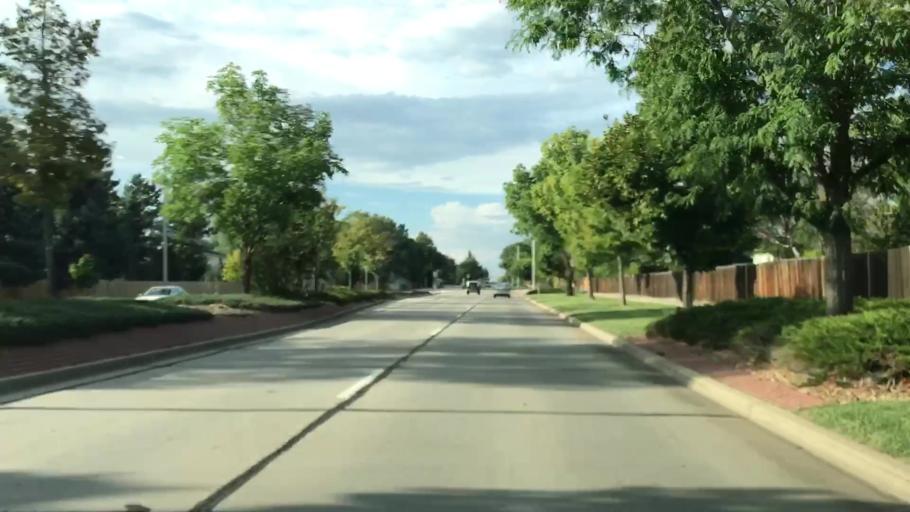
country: US
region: Colorado
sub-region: Boulder County
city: Longmont
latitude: 40.1981
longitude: -105.1309
